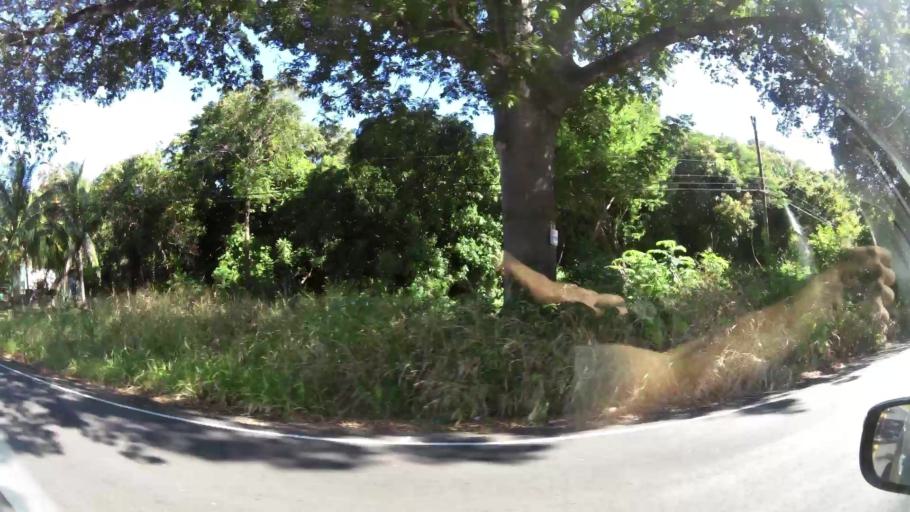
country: CR
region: Guanacaste
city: Sardinal
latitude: 10.4354
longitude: -85.7795
